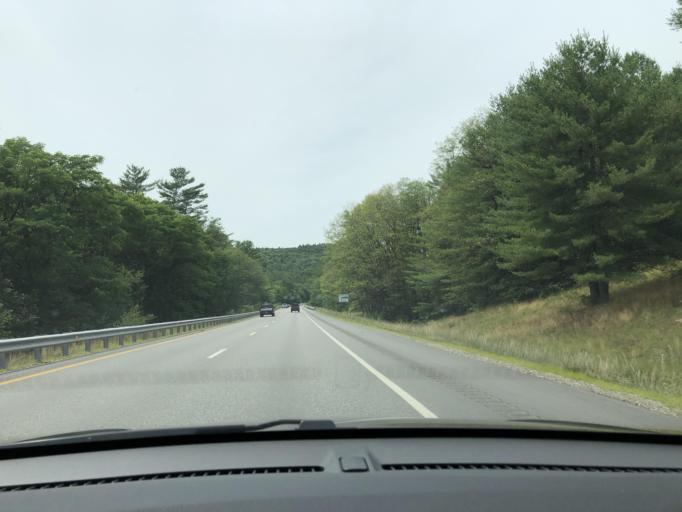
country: US
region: New Hampshire
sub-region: Merrimack County
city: Henniker
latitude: 43.2732
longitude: -71.7992
